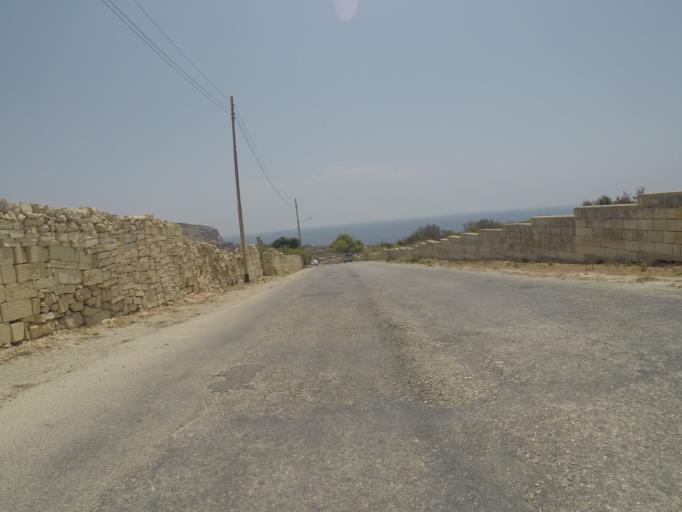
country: MT
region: Is-Siggiewi
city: Siggiewi
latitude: 35.8333
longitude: 14.4177
